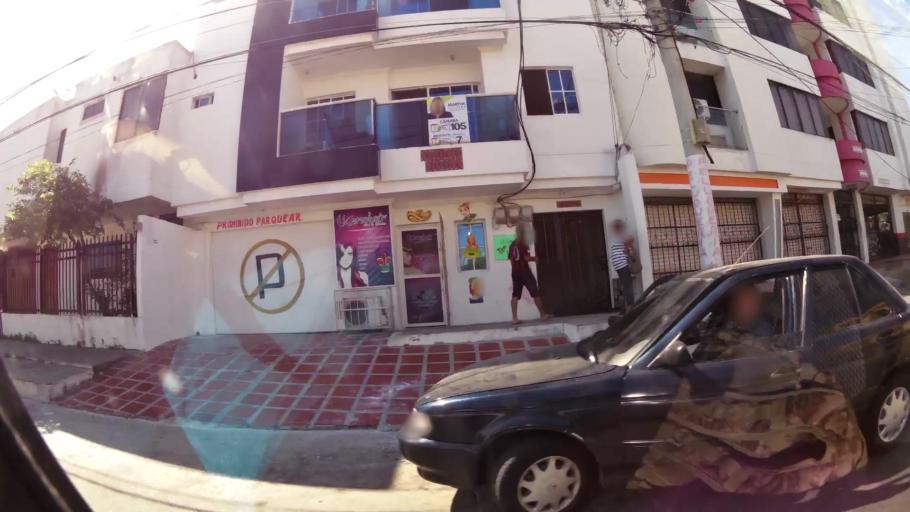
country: CO
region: Atlantico
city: Barranquilla
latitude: 10.9885
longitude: -74.7999
